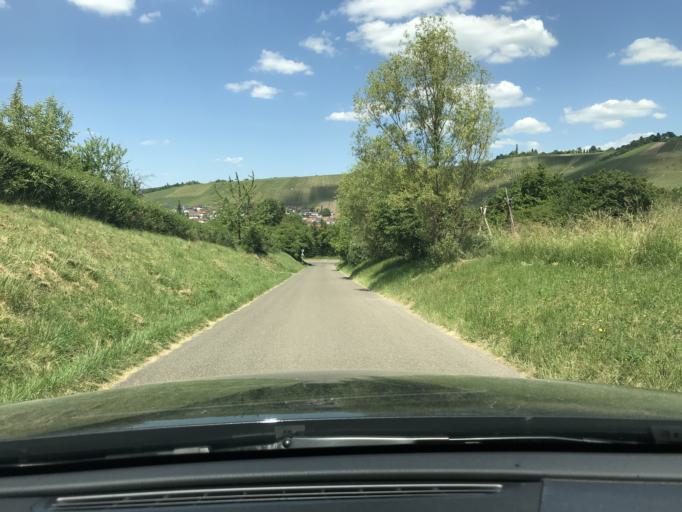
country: DE
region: Baden-Wuerttemberg
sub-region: Regierungsbezirk Stuttgart
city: Weinstadt-Endersbach
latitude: 48.7959
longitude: 9.3916
